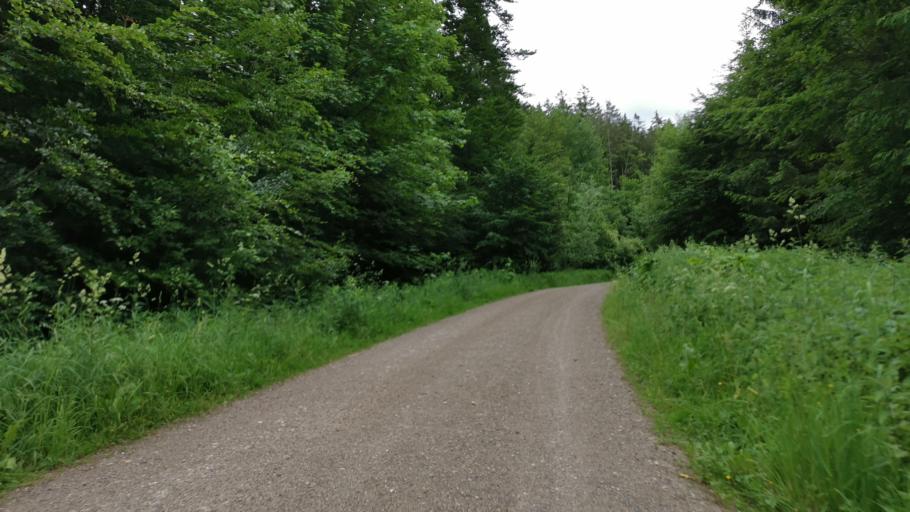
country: DE
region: Bavaria
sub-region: Upper Bavaria
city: Schaftlarn
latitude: 48.0078
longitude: 11.4391
